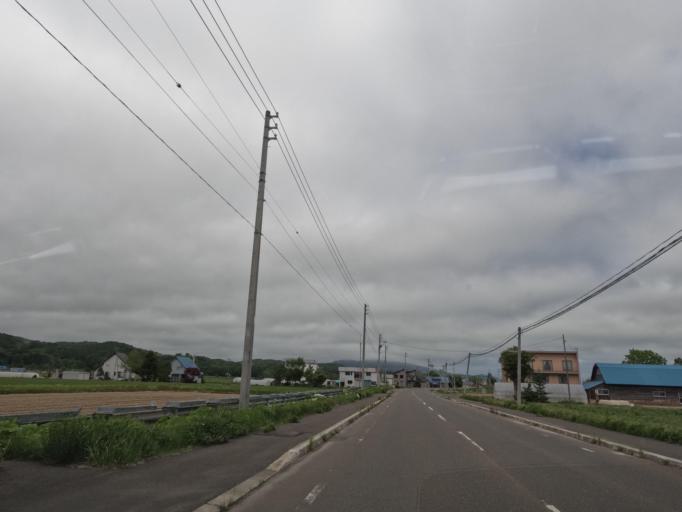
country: JP
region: Hokkaido
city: Tobetsu
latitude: 43.2414
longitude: 141.5136
